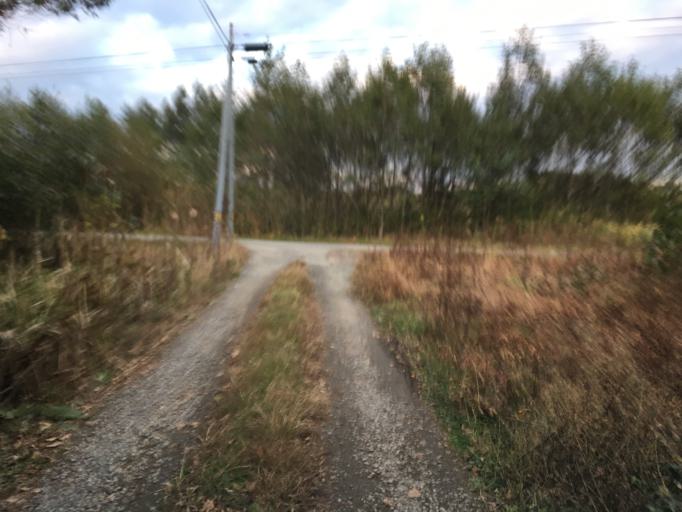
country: JP
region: Fukushima
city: Fukushima-shi
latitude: 37.7445
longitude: 140.3974
